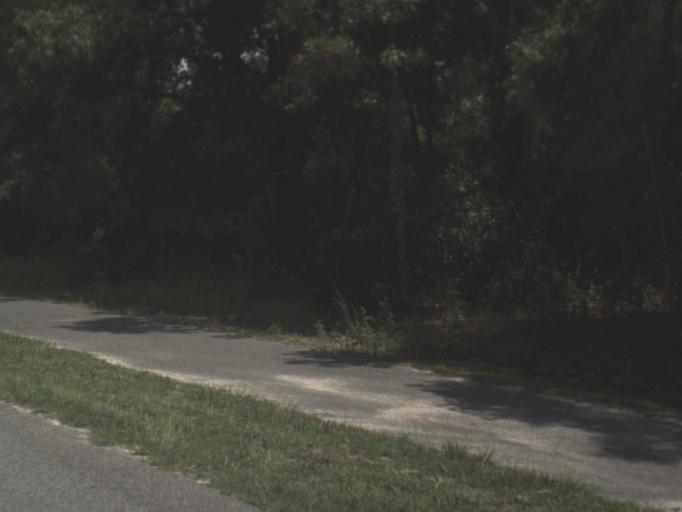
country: US
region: Florida
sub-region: Alachua County
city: High Springs
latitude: 29.9278
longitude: -82.7226
